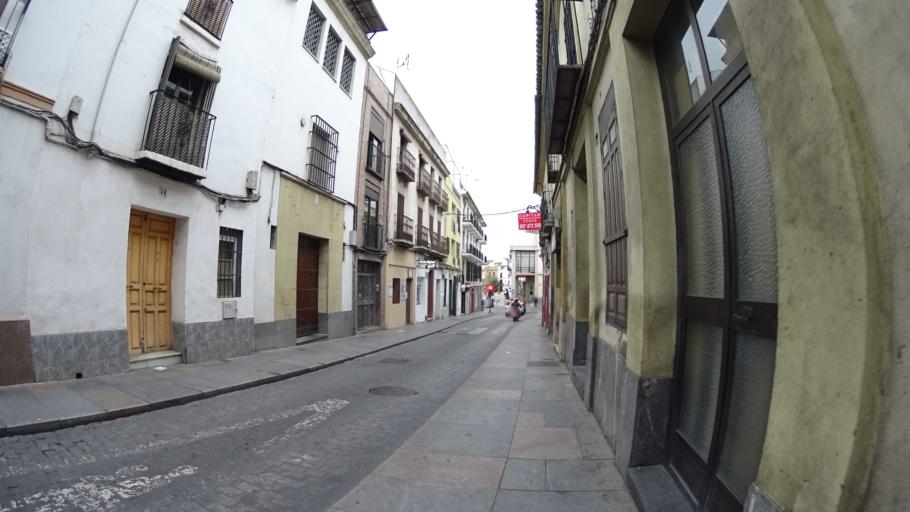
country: ES
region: Andalusia
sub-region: Province of Cordoba
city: Cordoba
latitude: 37.8861
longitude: -4.7763
